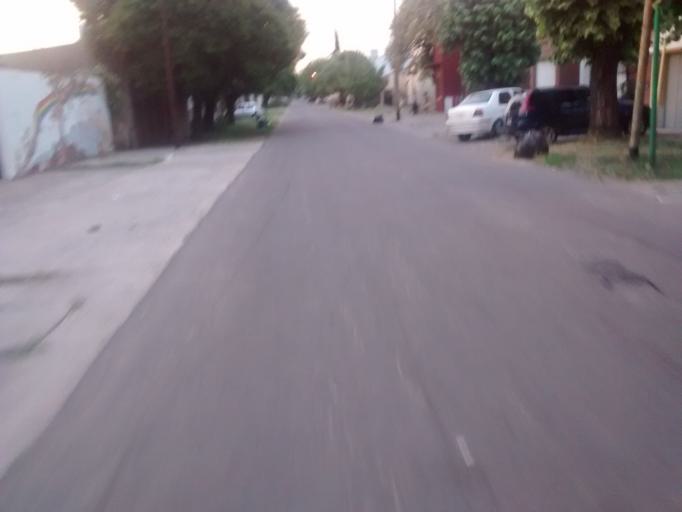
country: AR
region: Buenos Aires
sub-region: Partido de La Plata
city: La Plata
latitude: -34.9413
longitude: -57.9325
